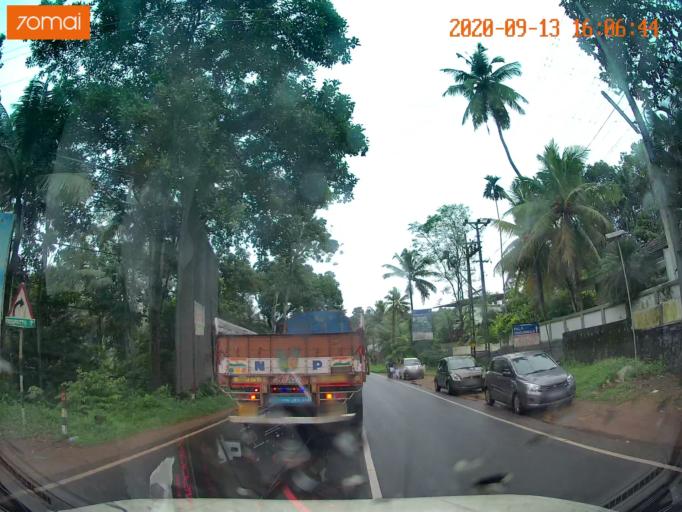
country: IN
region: Kerala
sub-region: Kottayam
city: Palackattumala
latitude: 9.6725
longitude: 76.5825
